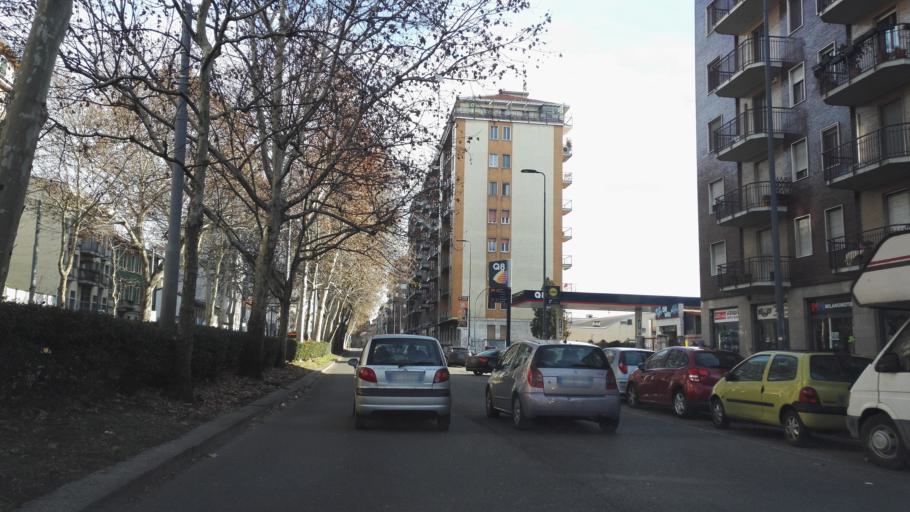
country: IT
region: Lombardy
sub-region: Citta metropolitana di Milano
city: Milano
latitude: 45.4437
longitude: 9.1734
